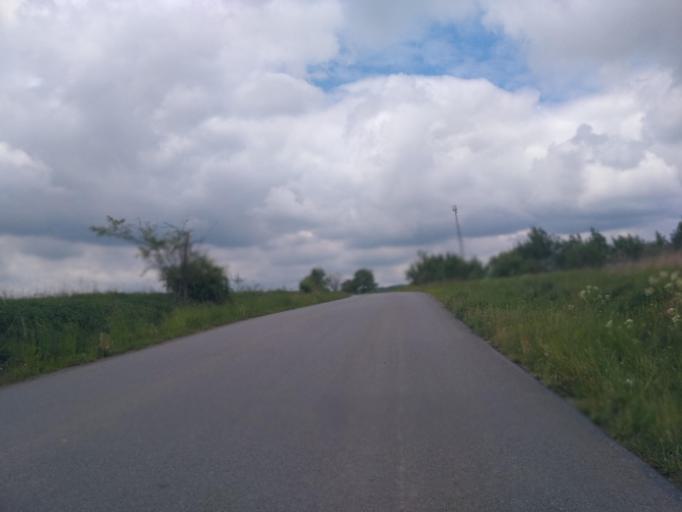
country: PL
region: Subcarpathian Voivodeship
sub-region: Powiat jasielski
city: Tarnowiec
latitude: 49.6673
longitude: 21.6007
